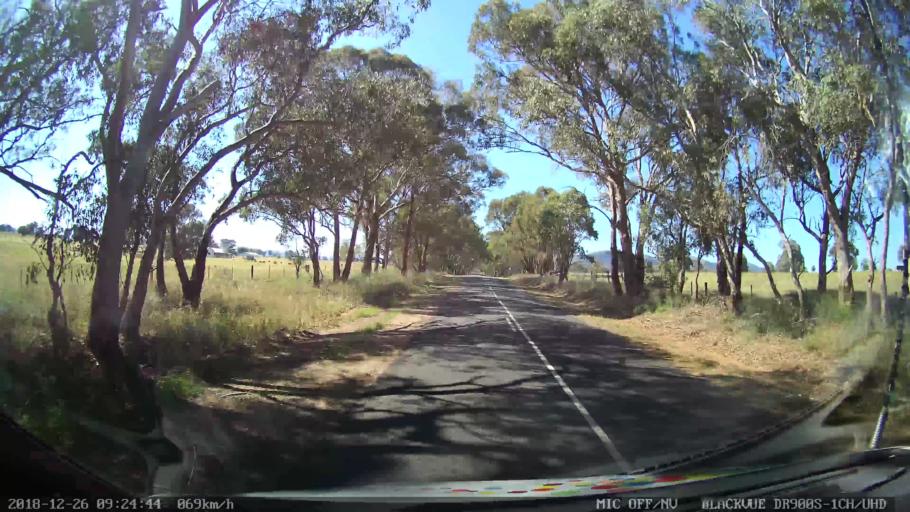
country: AU
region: New South Wales
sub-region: Mid-Western Regional
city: Kandos
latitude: -32.8131
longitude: 150.0007
